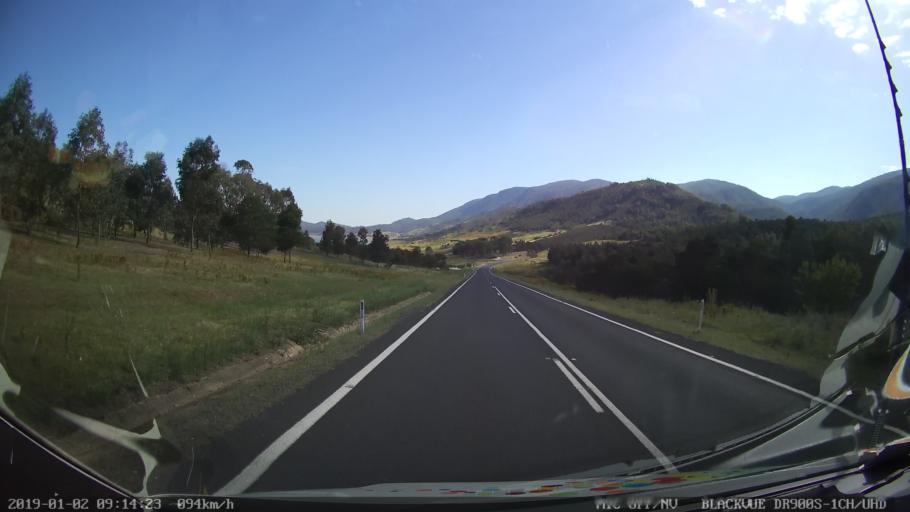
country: AU
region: New South Wales
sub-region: Tumut Shire
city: Tumut
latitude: -35.4779
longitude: 148.2735
